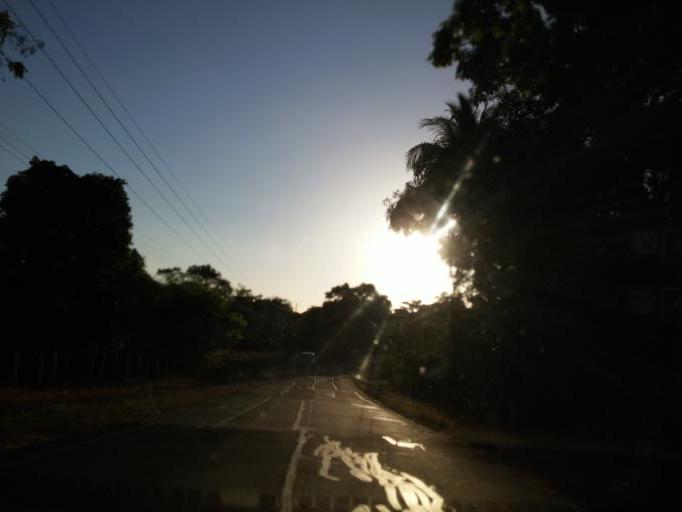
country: CR
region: Alajuela
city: Desamparados
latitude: 9.9408
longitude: -84.5158
